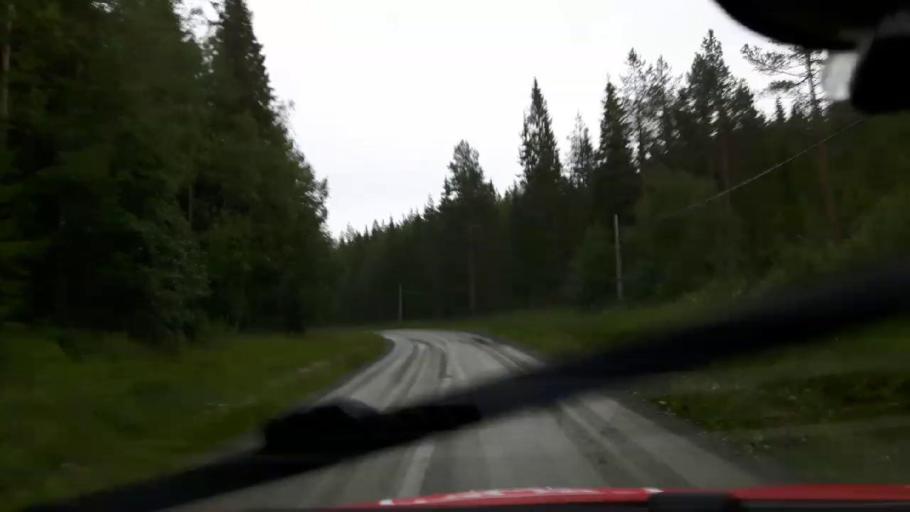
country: SE
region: Jaemtland
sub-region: OEstersunds Kommun
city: Brunflo
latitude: 62.8948
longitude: 14.8700
